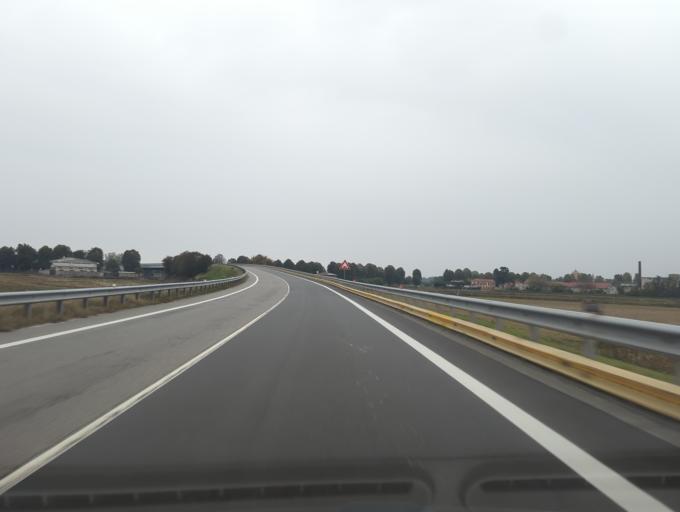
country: IT
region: Piedmont
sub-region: Provincia di Novara
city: Romentino
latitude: 45.4741
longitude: 8.7150
